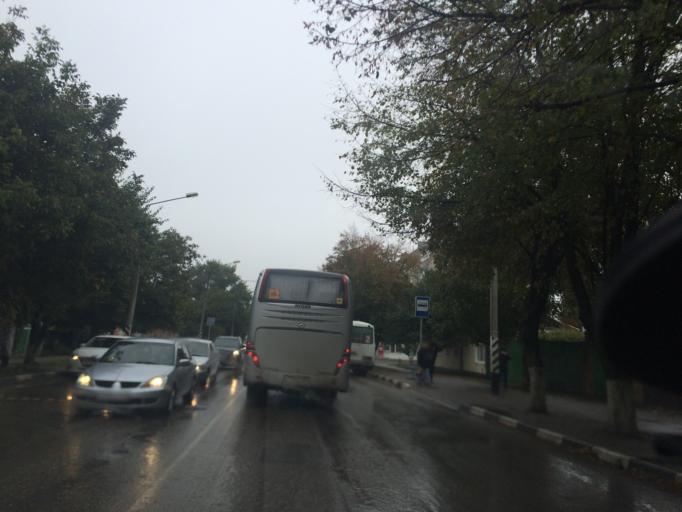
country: RU
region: Rostov
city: Azov
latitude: 47.0935
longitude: 39.4495
